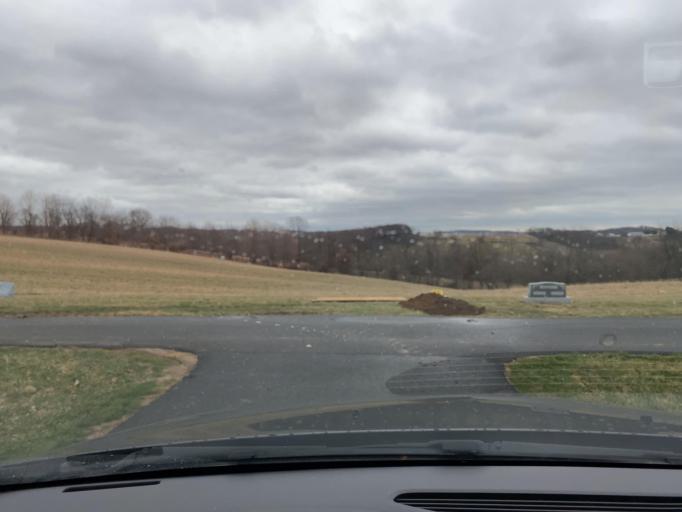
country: US
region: Ohio
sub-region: Wayne County
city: Apple Creek
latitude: 40.6794
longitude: -81.8648
